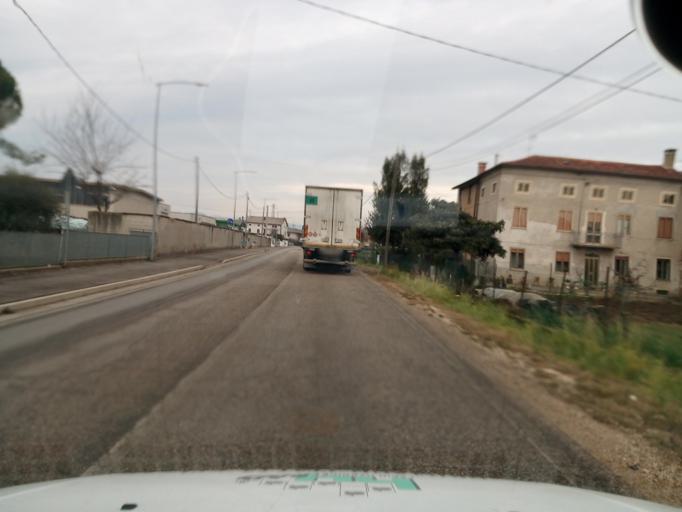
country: IT
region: Veneto
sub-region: Provincia di Vicenza
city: Tezze
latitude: 45.5449
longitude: 11.3799
